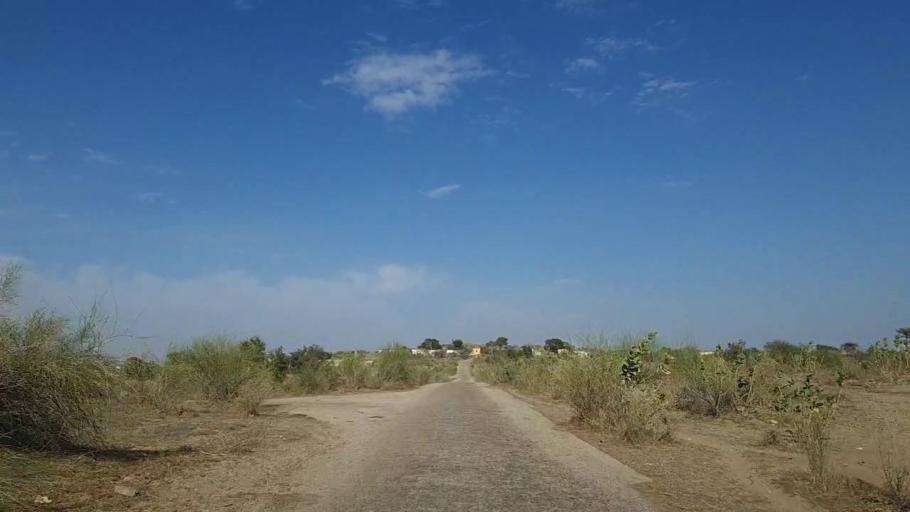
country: PK
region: Sindh
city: Naukot
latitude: 24.8496
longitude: 69.5601
